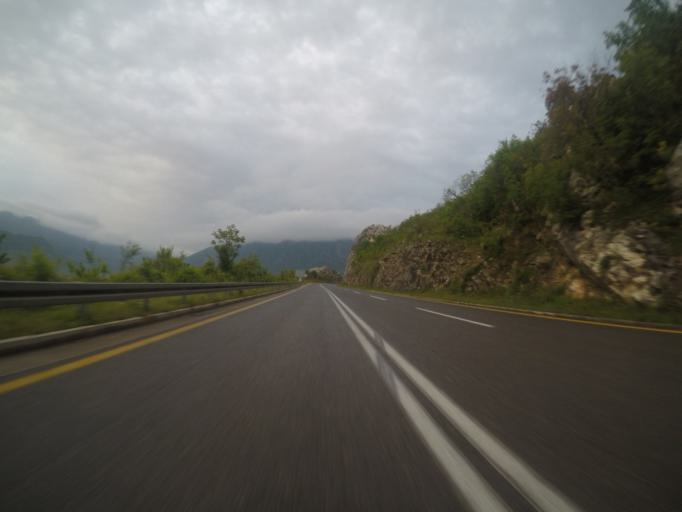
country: ME
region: Bar
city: Sutomore
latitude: 42.2222
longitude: 19.0512
